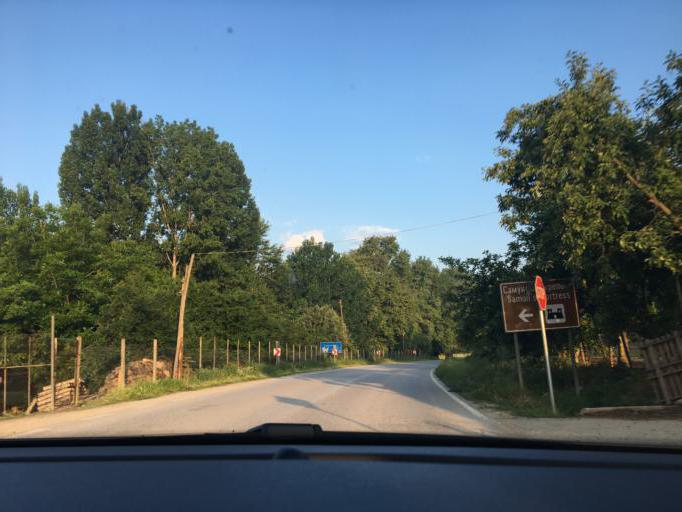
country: MK
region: Novo Selo
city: Novo Selo
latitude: 41.3947
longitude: 23.0361
